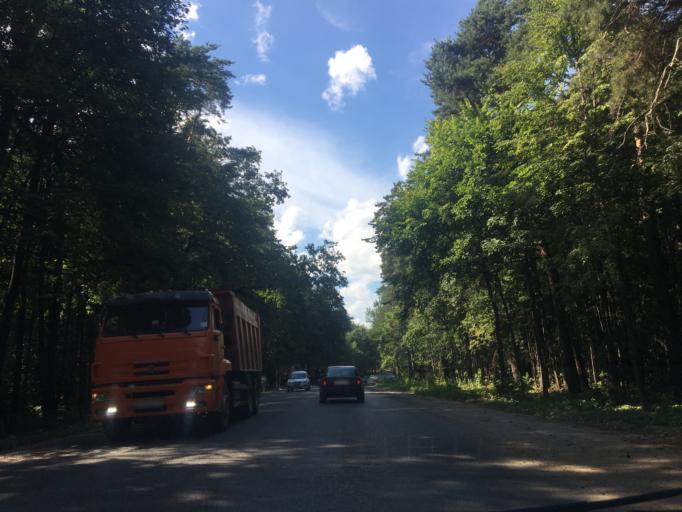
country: RU
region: Moscow
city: Zagor'ye
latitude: 55.5292
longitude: 37.6587
